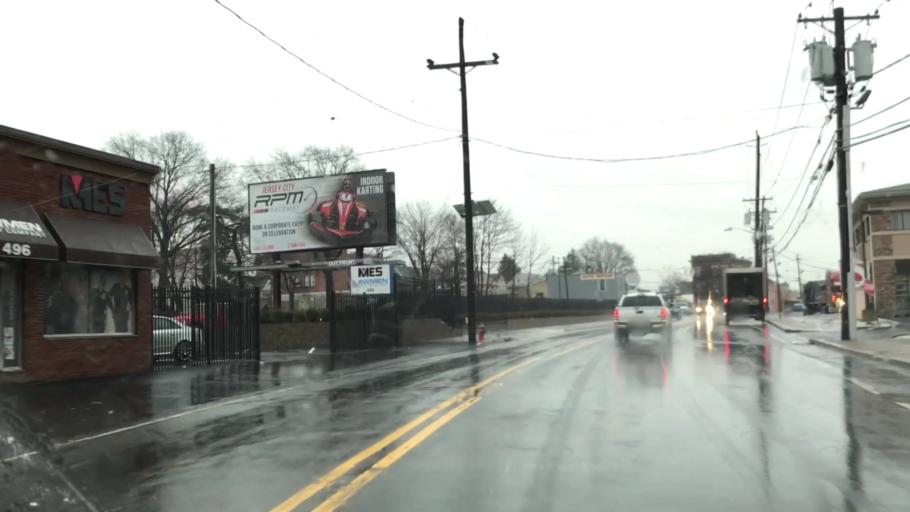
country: US
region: New Jersey
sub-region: Bergen County
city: Garfield
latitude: 40.8757
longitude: -74.1146
